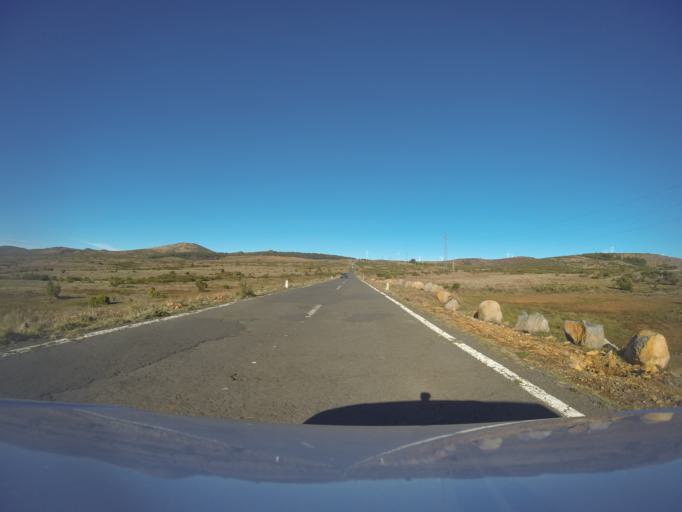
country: PT
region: Madeira
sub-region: Sao Vicente
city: Sao Vicente
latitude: 32.7617
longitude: -17.0883
